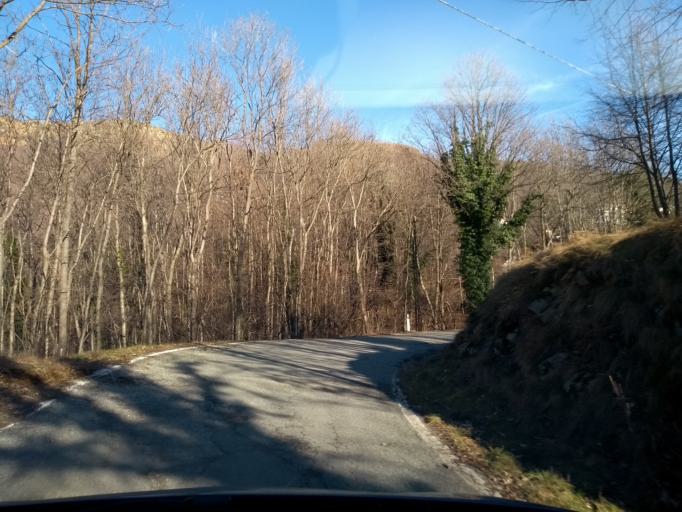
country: IT
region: Piedmont
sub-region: Provincia di Torino
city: Pessinetto
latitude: 45.2844
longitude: 7.4289
